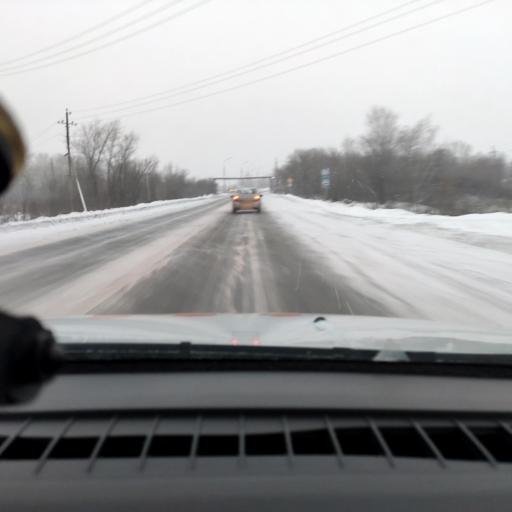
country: RU
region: Samara
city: Otradnyy
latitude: 53.3495
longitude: 51.3222
